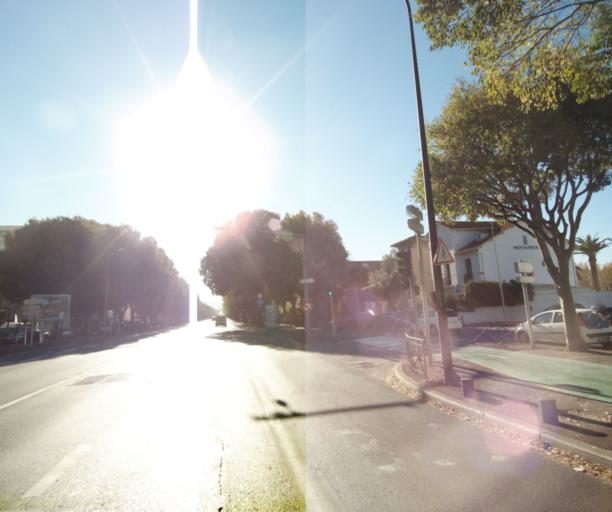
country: FR
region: Provence-Alpes-Cote d'Azur
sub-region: Departement des Bouches-du-Rhone
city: Marseille 08
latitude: 43.2654
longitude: 5.3953
